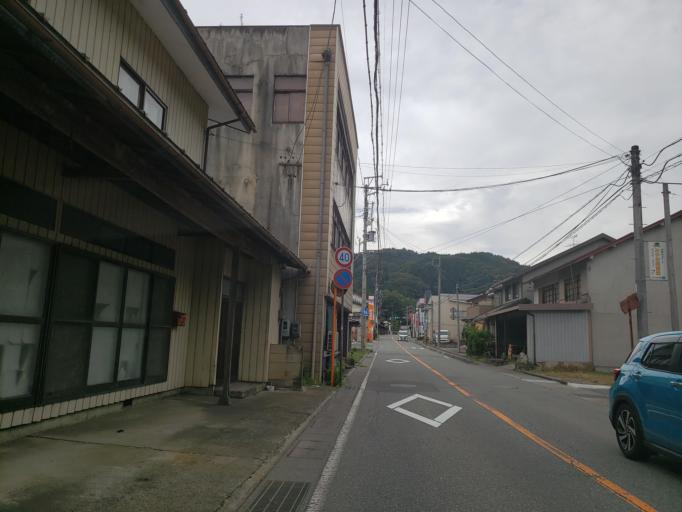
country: JP
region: Nagano
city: Nagano-shi
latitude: 36.6095
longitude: 138.0354
